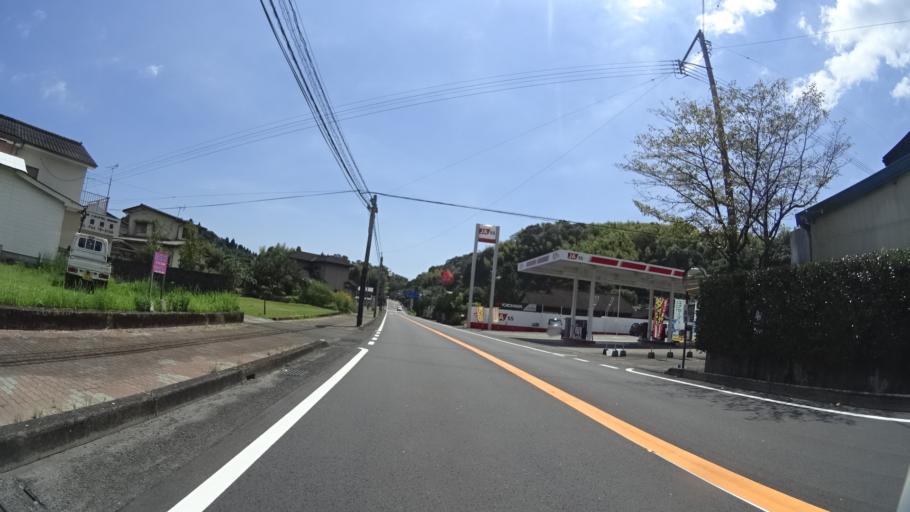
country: JP
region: Kagoshima
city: Kokubu-matsuki
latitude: 31.8539
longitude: 130.7529
